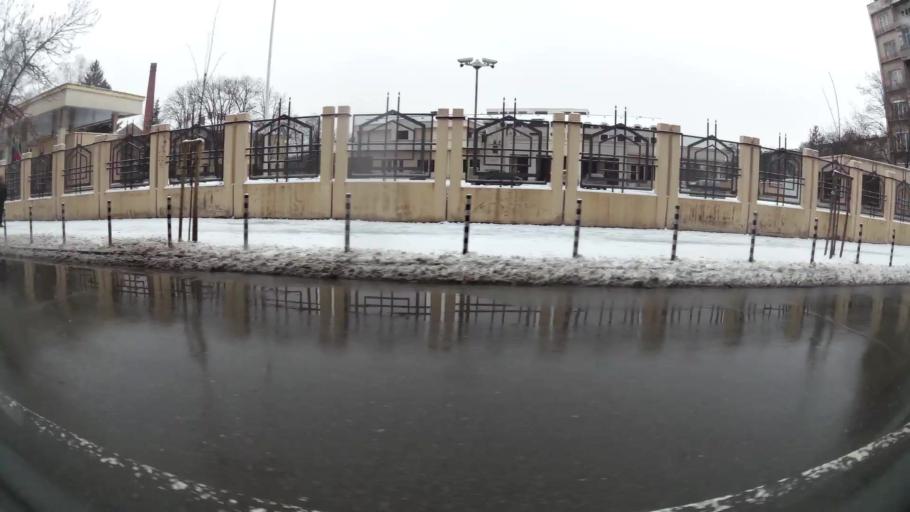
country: BG
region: Sofia-Capital
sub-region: Stolichna Obshtina
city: Sofia
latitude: 42.6915
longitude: 23.3512
